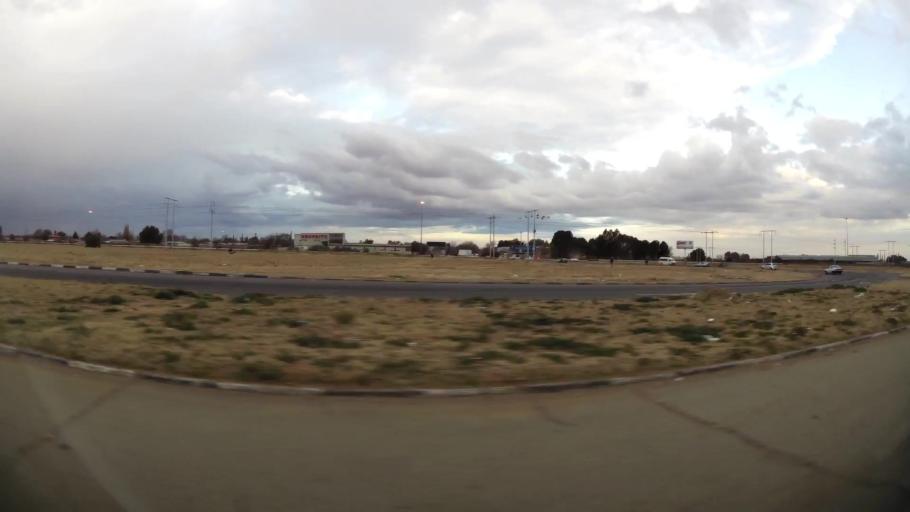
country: ZA
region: Orange Free State
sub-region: Lejweleputswa District Municipality
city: Welkom
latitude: -27.9747
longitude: 26.7746
